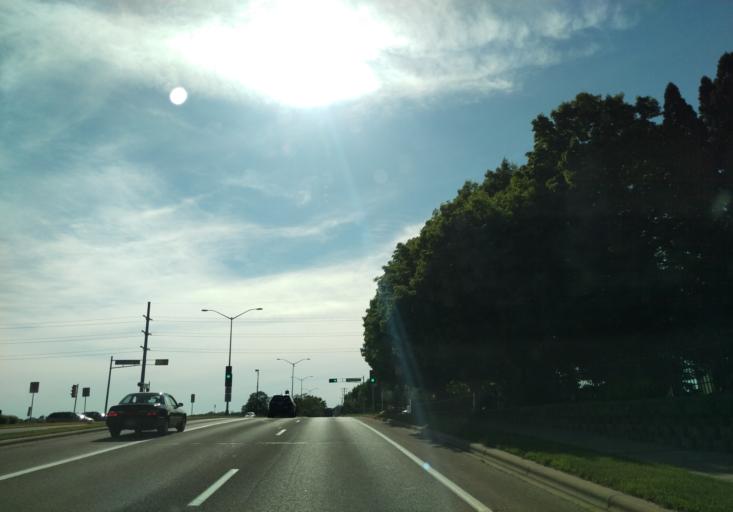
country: US
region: Wisconsin
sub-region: Dane County
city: Middleton
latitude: 43.0749
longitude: -89.5361
